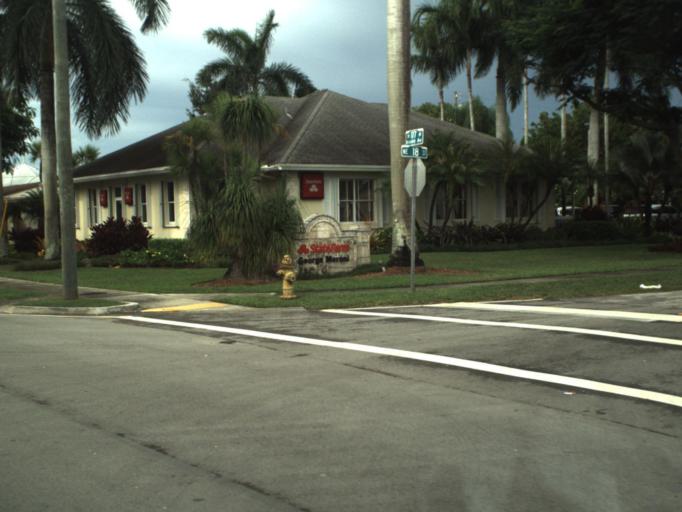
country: US
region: Florida
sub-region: Miami-Dade County
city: Homestead
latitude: 25.4871
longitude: -80.4775
